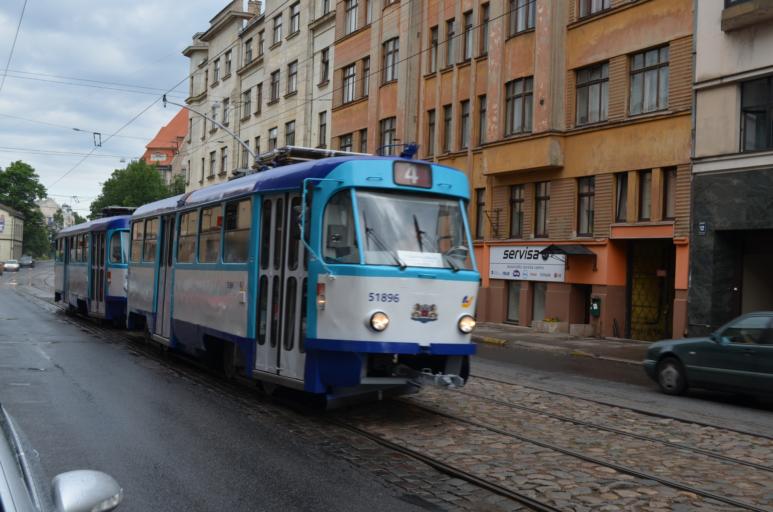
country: LV
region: Riga
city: Riga
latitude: 56.9450
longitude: 24.0752
